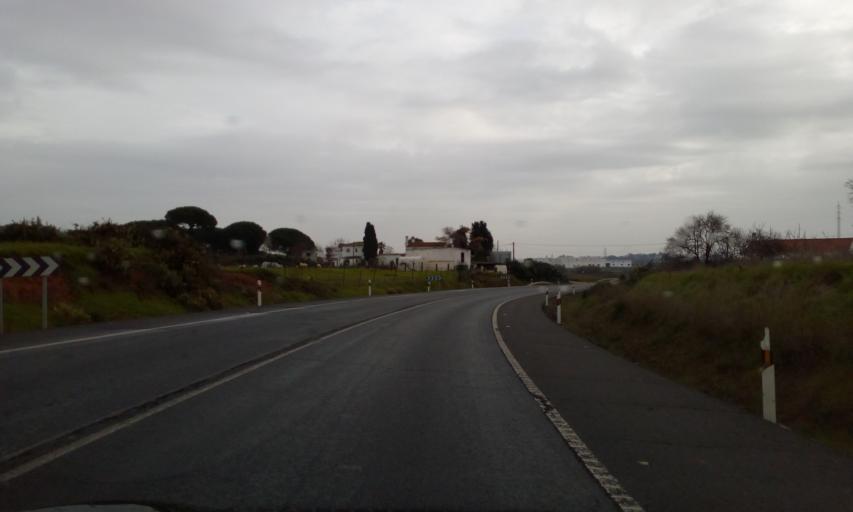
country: ES
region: Andalusia
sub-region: Provincia de Huelva
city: Cartaya
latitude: 37.2849
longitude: -7.1798
